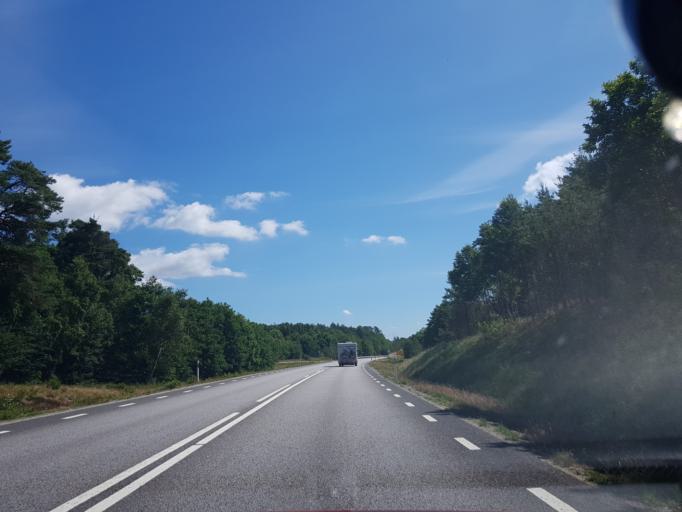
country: SE
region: Vaestra Goetaland
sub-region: Orust
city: Henan
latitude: 58.1548
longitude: 11.5412
